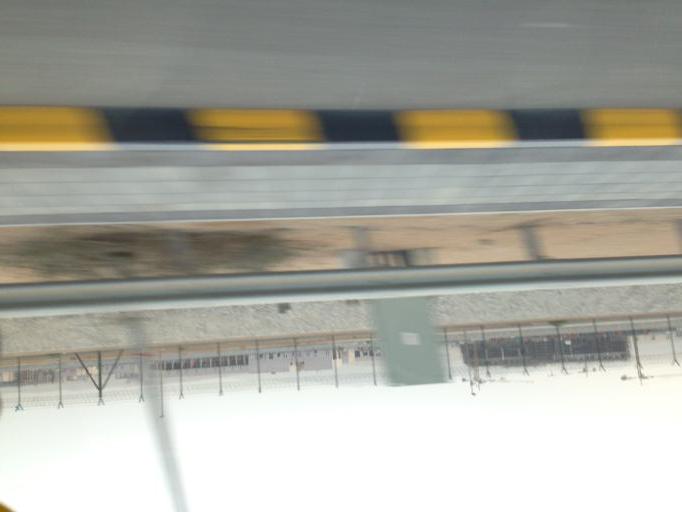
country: OM
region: Muhafazat Masqat
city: Bawshar
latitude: 23.6096
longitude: 58.3059
